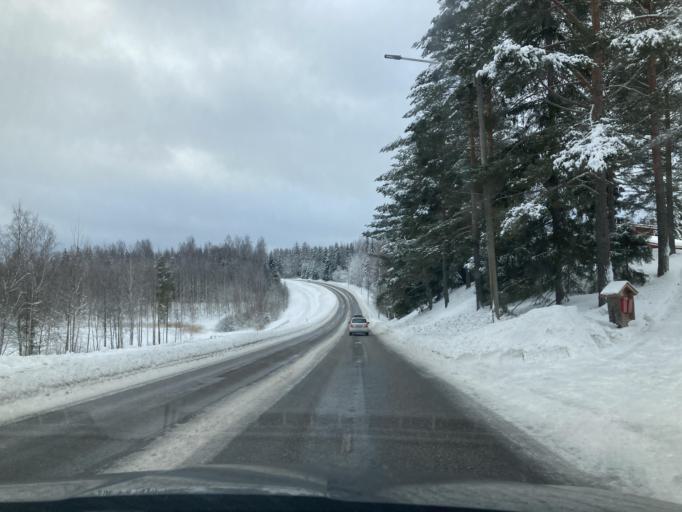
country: FI
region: Central Finland
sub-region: Jaemsae
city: Kuhmoinen
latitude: 61.5574
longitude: 25.1595
